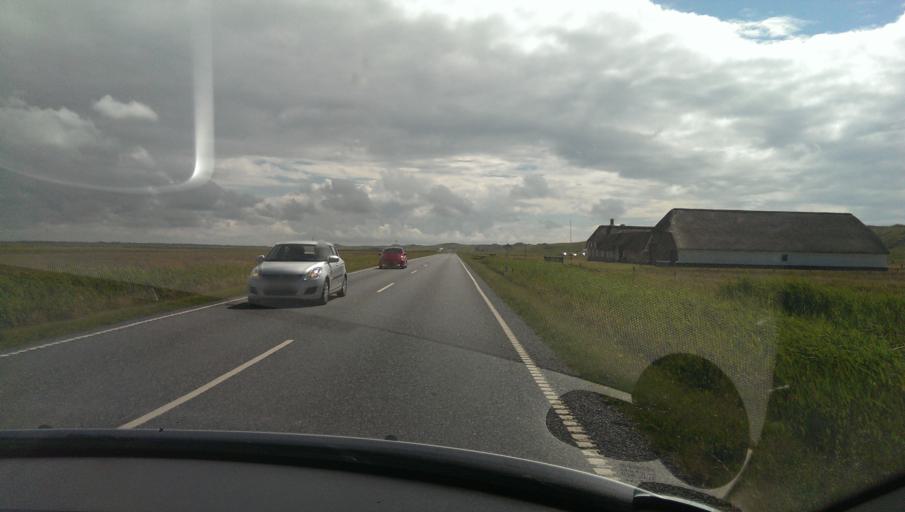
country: DK
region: Central Jutland
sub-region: Ringkobing-Skjern Kommune
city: Ringkobing
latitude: 56.1952
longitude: 8.1293
